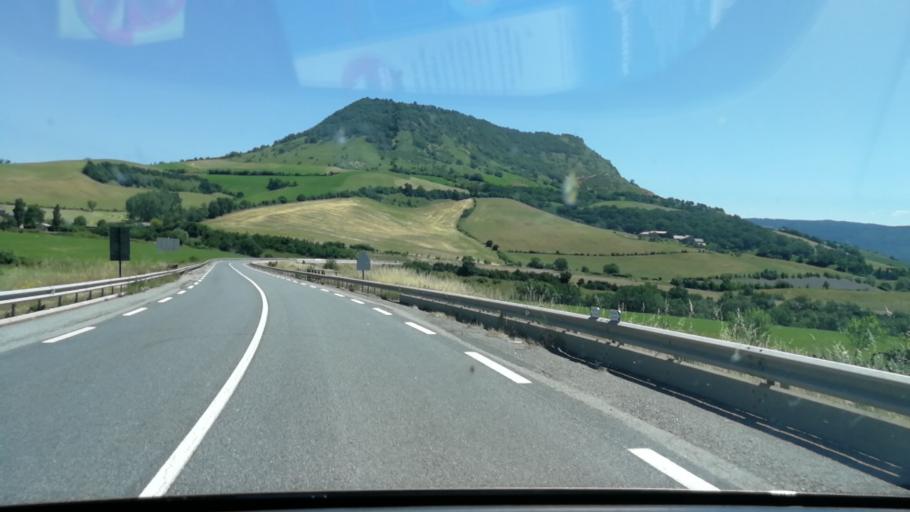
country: FR
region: Midi-Pyrenees
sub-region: Departement de l'Aveyron
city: Creissels
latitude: 44.1335
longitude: 3.0355
